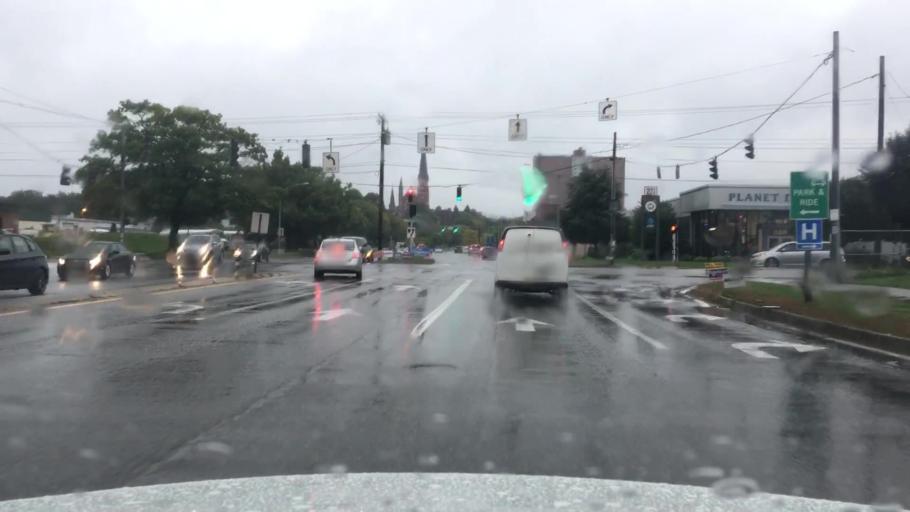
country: US
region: Maine
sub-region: Cumberland County
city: Portland
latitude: 43.6654
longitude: -70.2605
